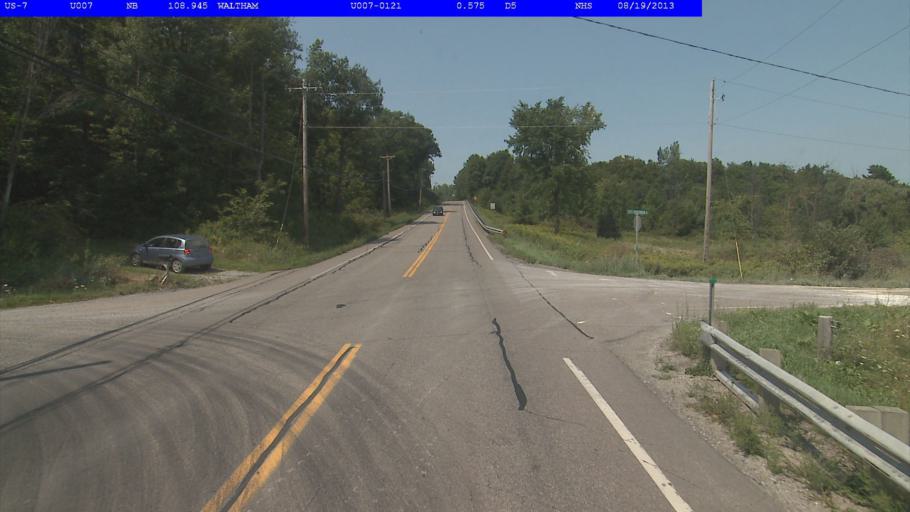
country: US
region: Vermont
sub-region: Addison County
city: Vergennes
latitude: 44.1538
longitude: -73.2180
